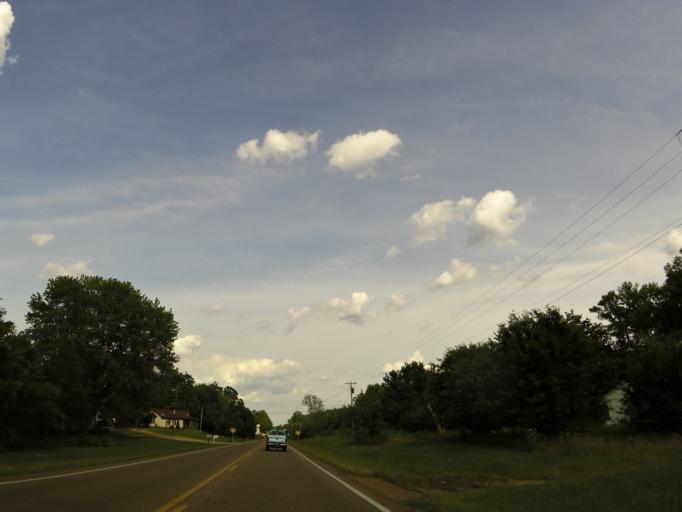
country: US
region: Tennessee
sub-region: Carroll County
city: Bruceton
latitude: 36.0372
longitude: -88.2957
